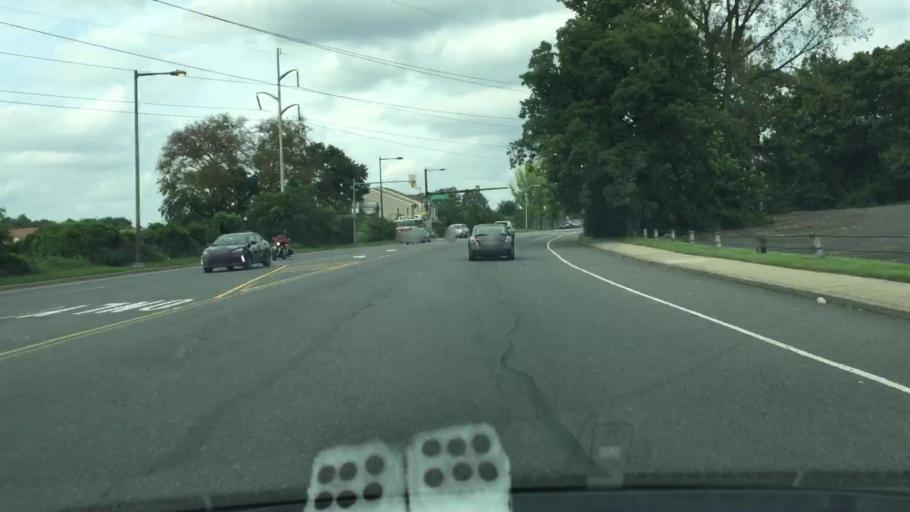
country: US
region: Pennsylvania
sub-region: Montgomery County
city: Rockledge
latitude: 40.0814
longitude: -75.0414
